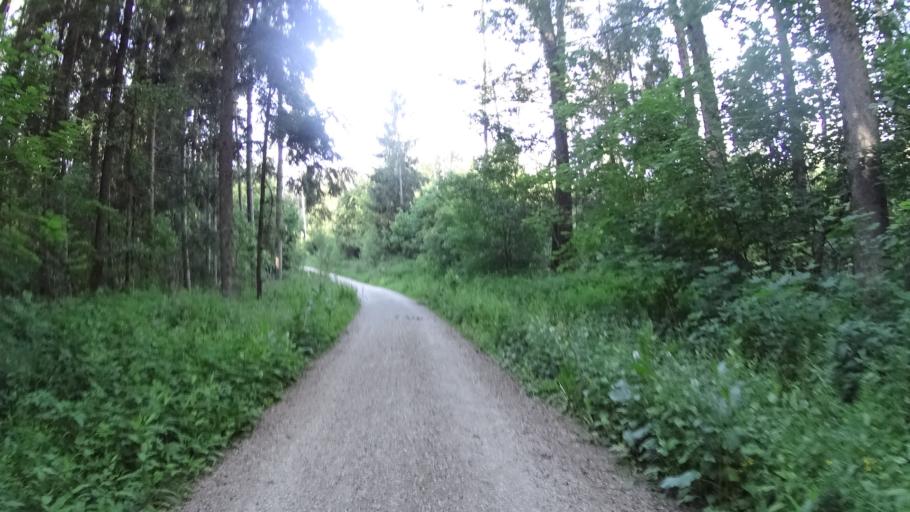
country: DE
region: Bavaria
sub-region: Regierungsbezirk Mittelfranken
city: Lichtenau
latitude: 49.1542
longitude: 10.3920
